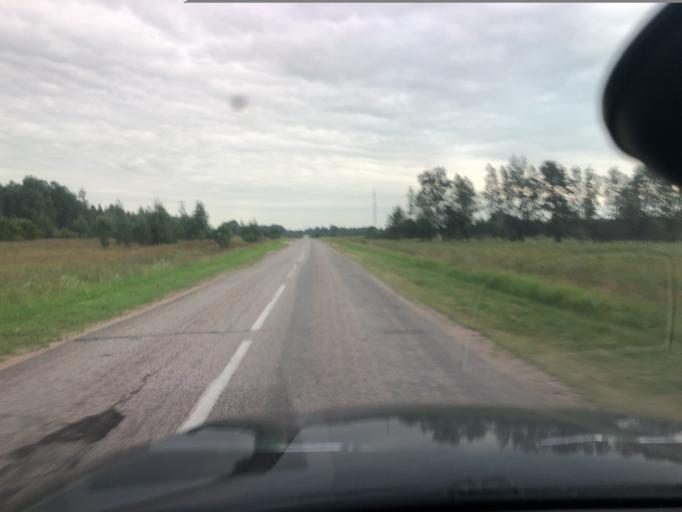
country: RU
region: Jaroslavl
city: Petrovsk
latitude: 57.0026
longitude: 39.0282
